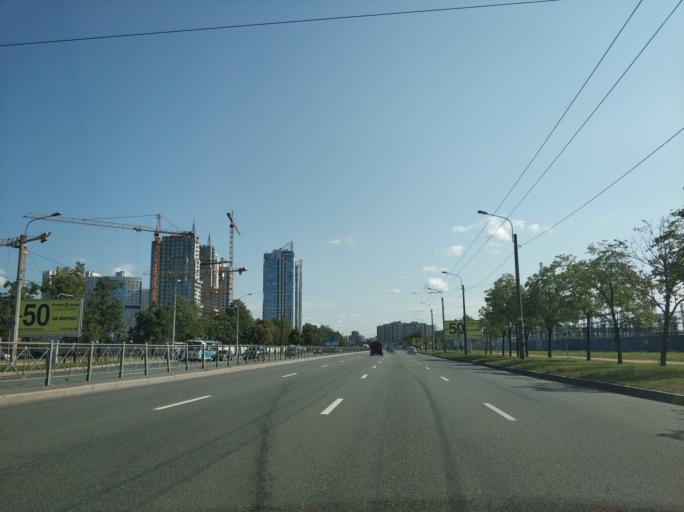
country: RU
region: St.-Petersburg
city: Kupchino
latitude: 59.8524
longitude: 30.3403
